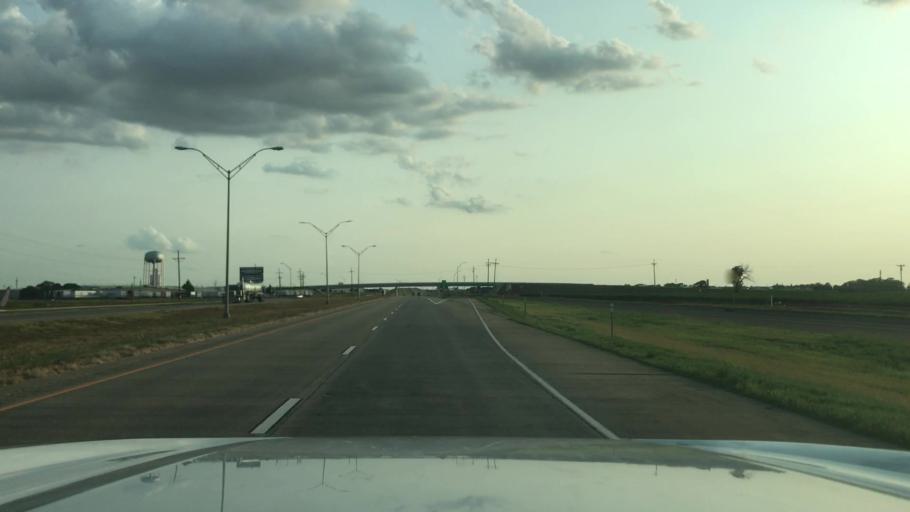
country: US
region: Texas
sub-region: Hale County
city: Seth Ward
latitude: 34.2226
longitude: -101.7217
